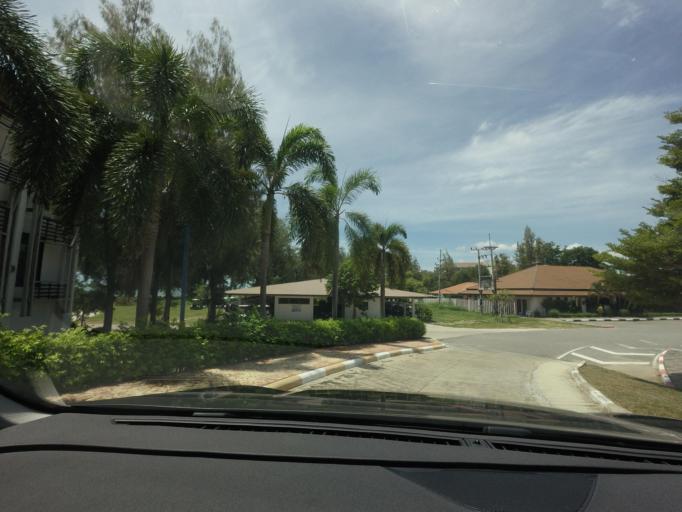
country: TH
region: Prachuap Khiri Khan
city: Hua Hin
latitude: 12.5055
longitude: 99.9740
